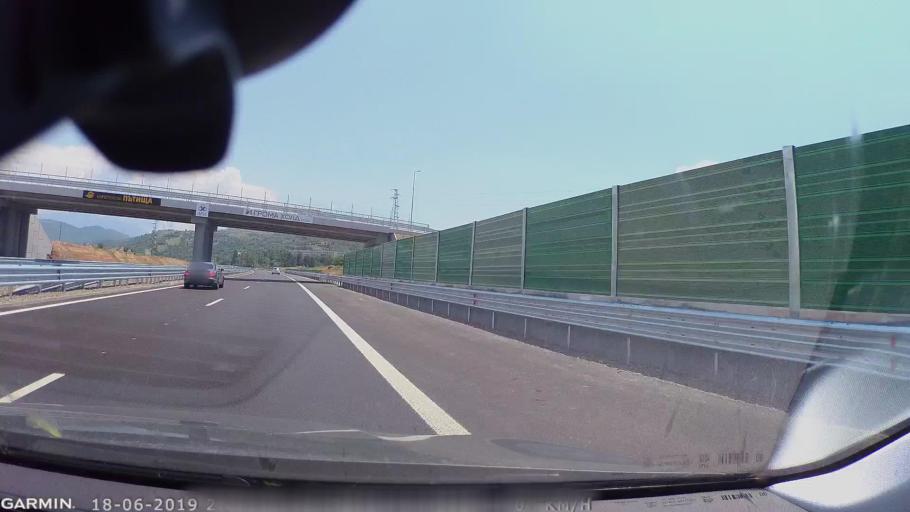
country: BG
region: Blagoevgrad
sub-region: Obshtina Blagoevgrad
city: Blagoevgrad
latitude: 41.9866
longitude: 23.0569
